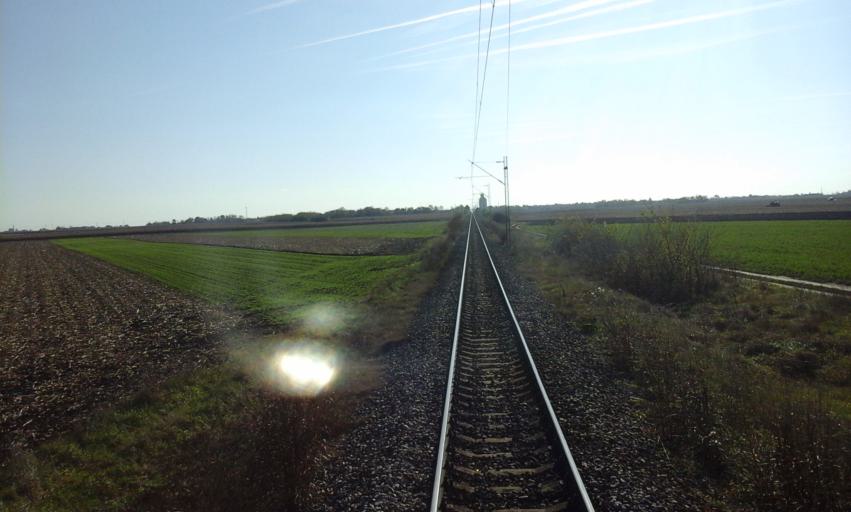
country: RS
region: Autonomna Pokrajina Vojvodina
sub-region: Severnobacki Okrug
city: Subotica
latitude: 45.9627
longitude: 19.6718
